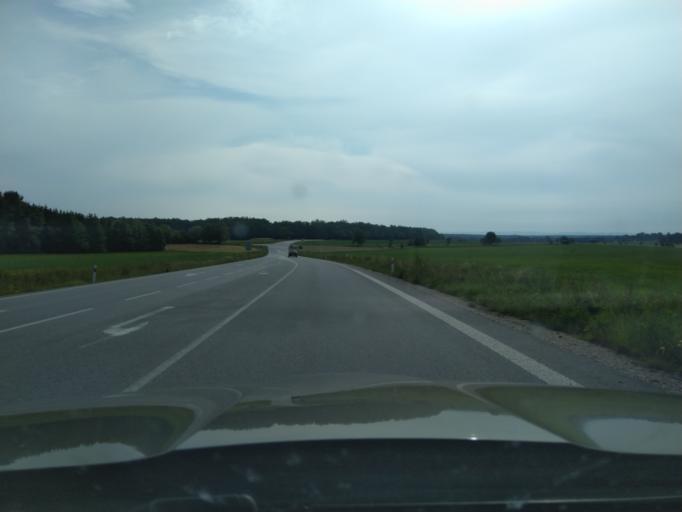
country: CZ
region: Jihocesky
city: Netolice
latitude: 49.0295
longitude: 14.2717
